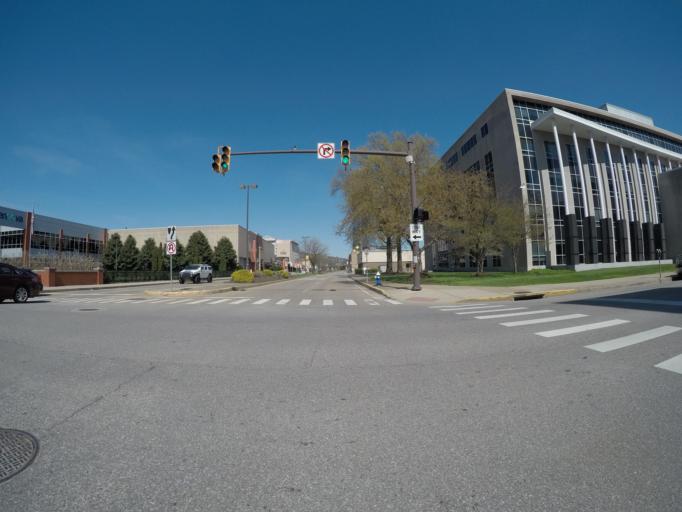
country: US
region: West Virginia
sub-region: Kanawha County
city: Charleston
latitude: 38.3519
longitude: -81.6374
